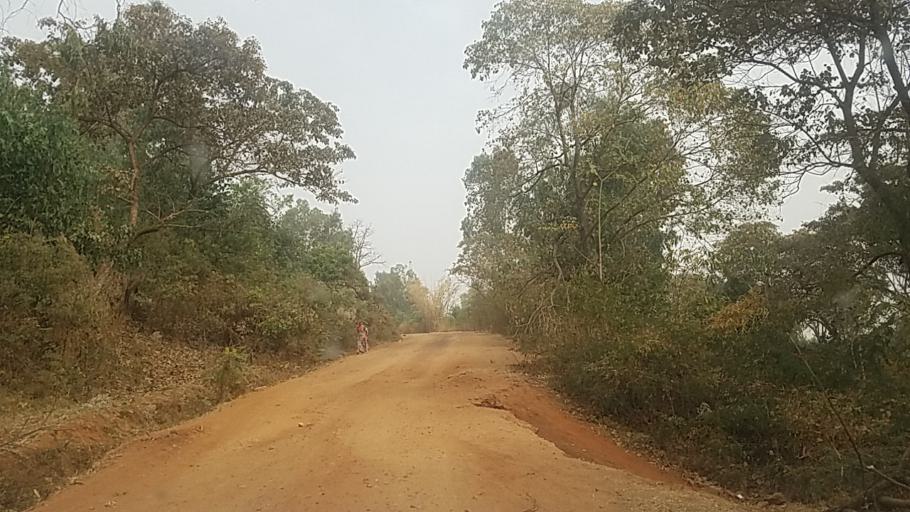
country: ET
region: Amhara
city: Bure
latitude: 10.8580
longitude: 36.3798
